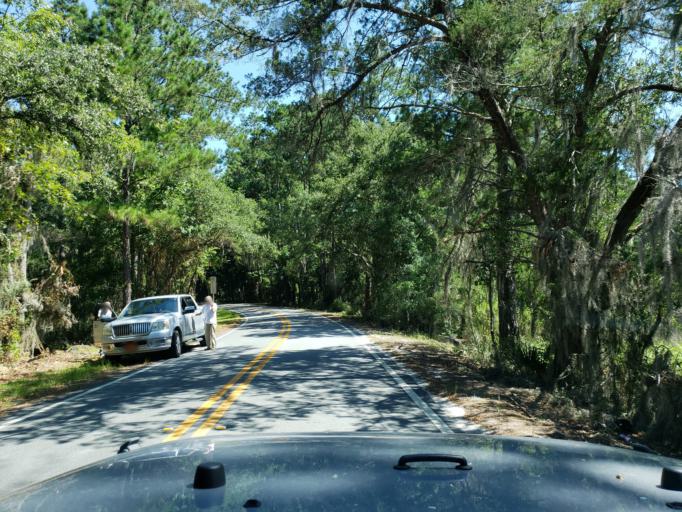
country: US
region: Georgia
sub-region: Chatham County
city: Georgetown
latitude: 31.9672
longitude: -81.2184
